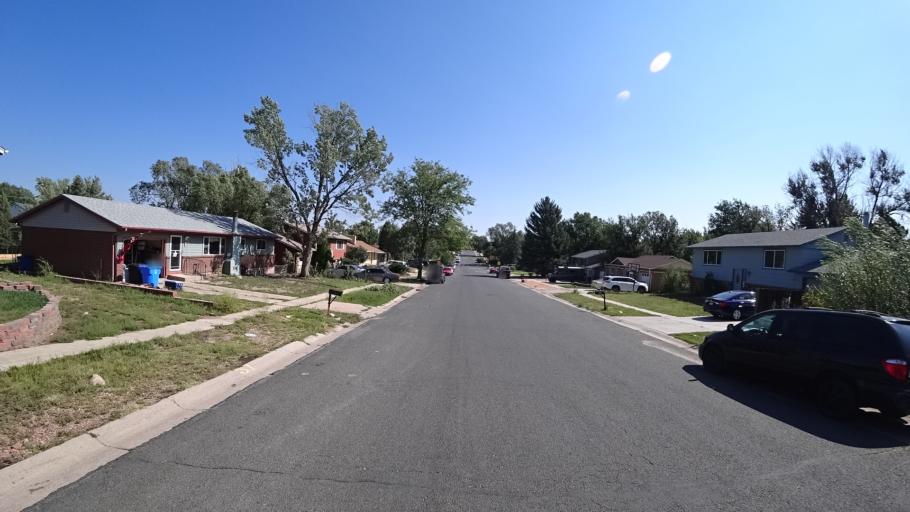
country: US
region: Colorado
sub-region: El Paso County
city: Stratmoor
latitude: 38.8087
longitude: -104.7756
